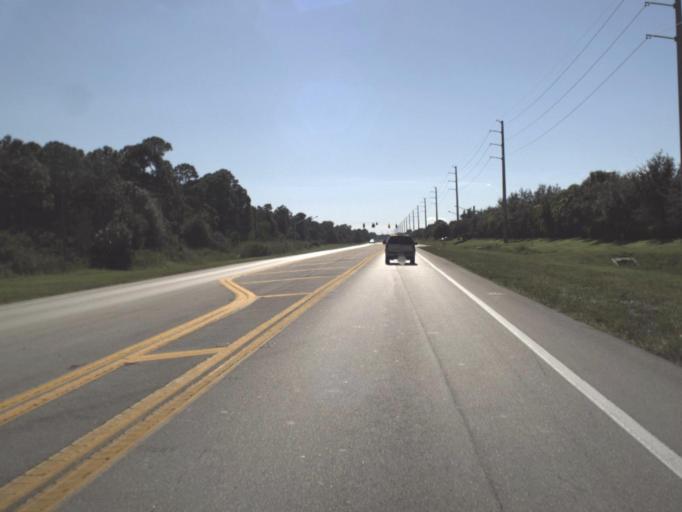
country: US
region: Florida
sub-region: Lee County
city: Gateway
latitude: 26.6105
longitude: -81.7585
